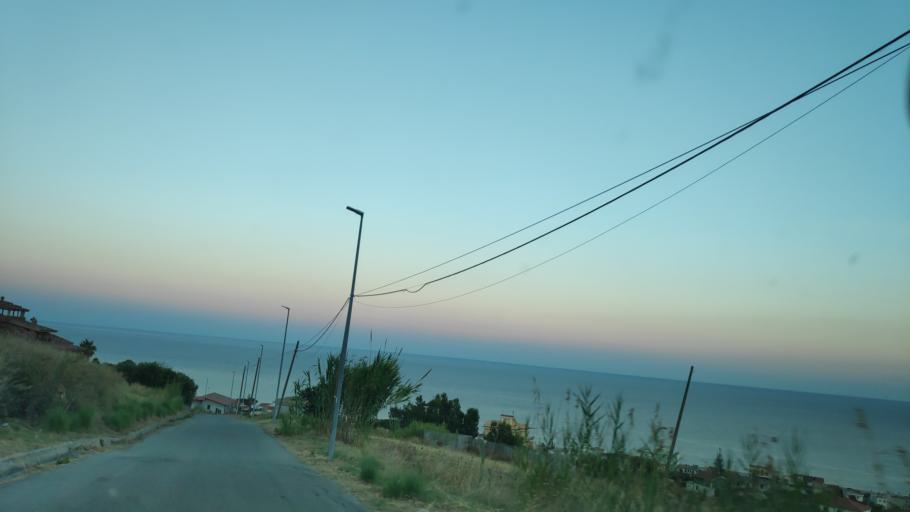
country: IT
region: Calabria
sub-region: Provincia di Reggio Calabria
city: Riace Marina
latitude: 38.3930
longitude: 16.5256
